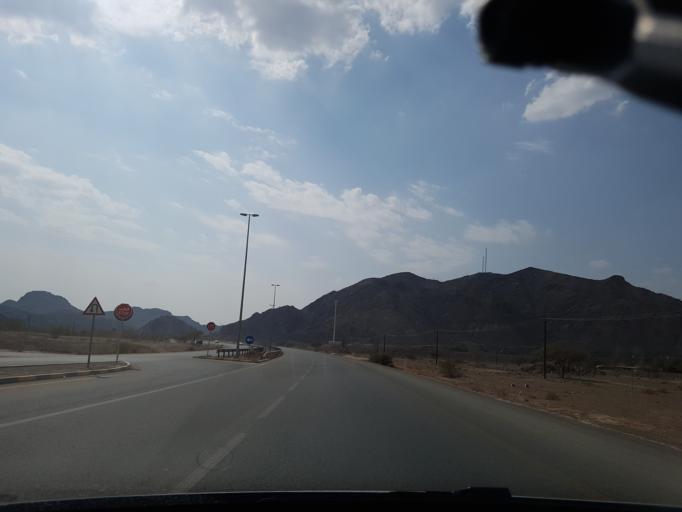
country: AE
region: Al Fujayrah
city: Dibba Al-Fujairah
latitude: 25.4981
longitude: 56.0632
